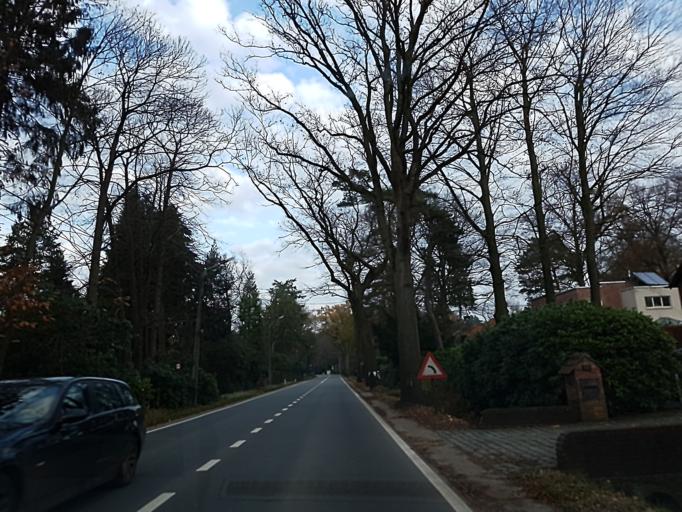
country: BE
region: Flanders
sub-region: Provincie Antwerpen
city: Kalmthout
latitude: 51.3555
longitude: 4.4596
